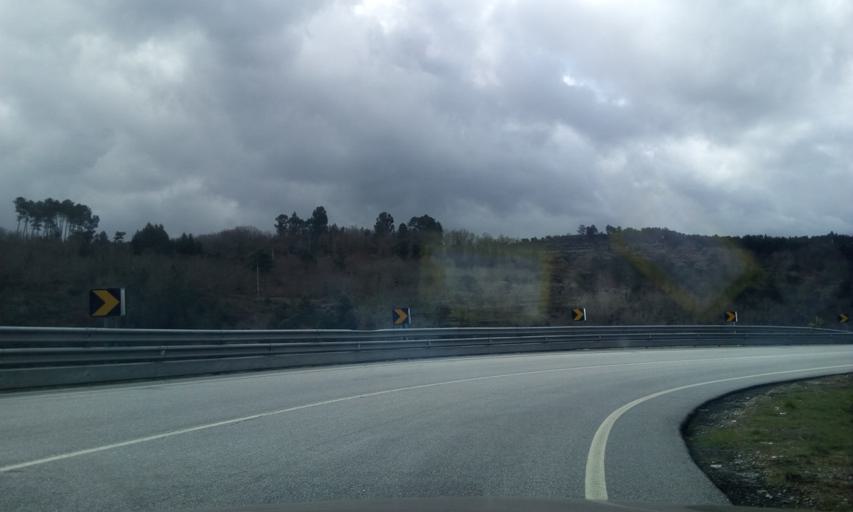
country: PT
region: Viseu
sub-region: Mangualde
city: Mangualde
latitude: 40.6475
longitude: -7.7291
